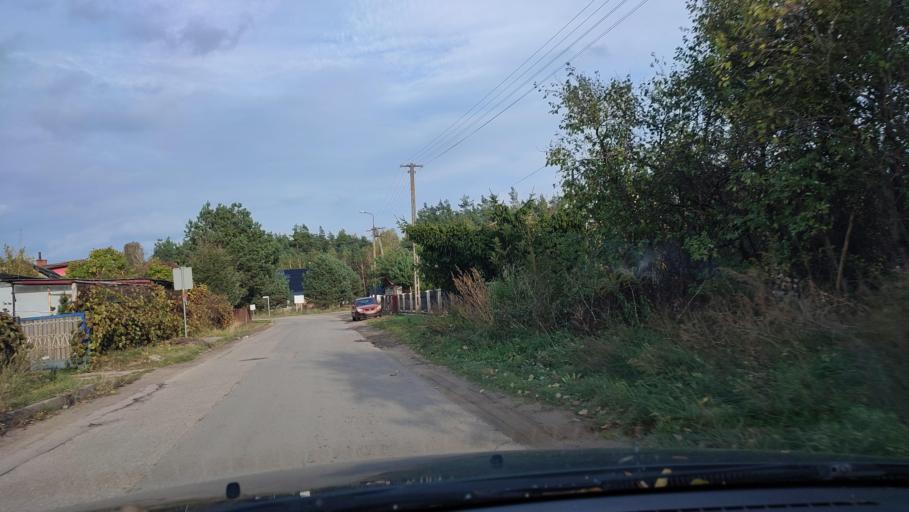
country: PL
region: Masovian Voivodeship
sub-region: Powiat mlawski
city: Mlawa
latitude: 53.1404
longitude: 20.3695
